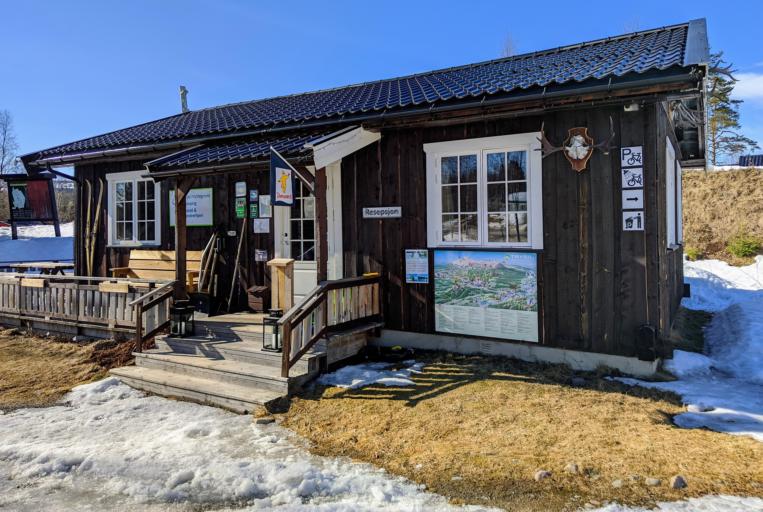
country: NO
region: Hedmark
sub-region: Trysil
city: Innbygda
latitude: 61.2931
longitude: 12.2834
